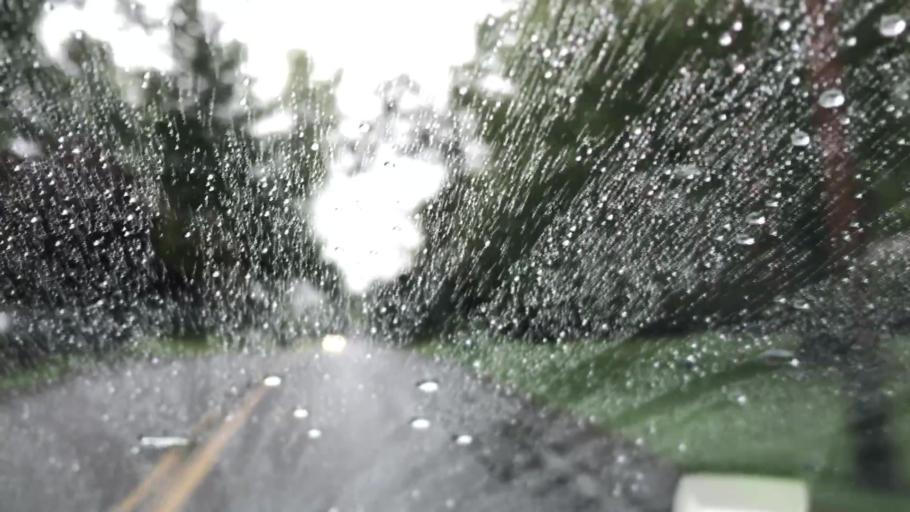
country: US
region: Pennsylvania
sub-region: Allegheny County
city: Franklin Park
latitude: 40.5855
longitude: -80.0719
